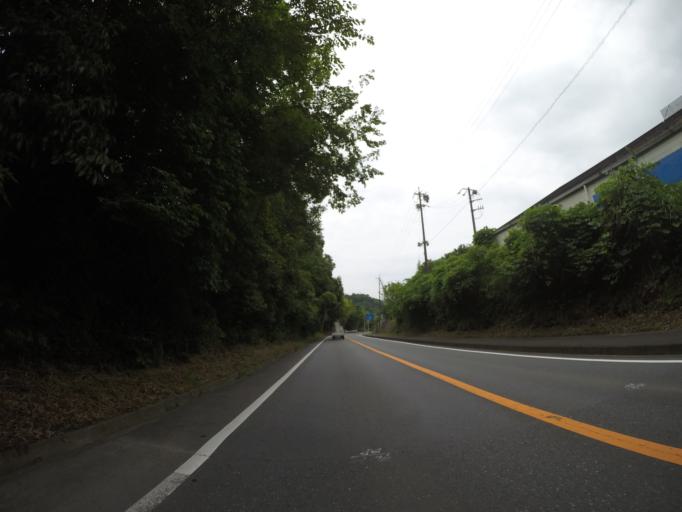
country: JP
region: Shizuoka
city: Fujinomiya
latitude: 35.1948
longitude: 138.5859
